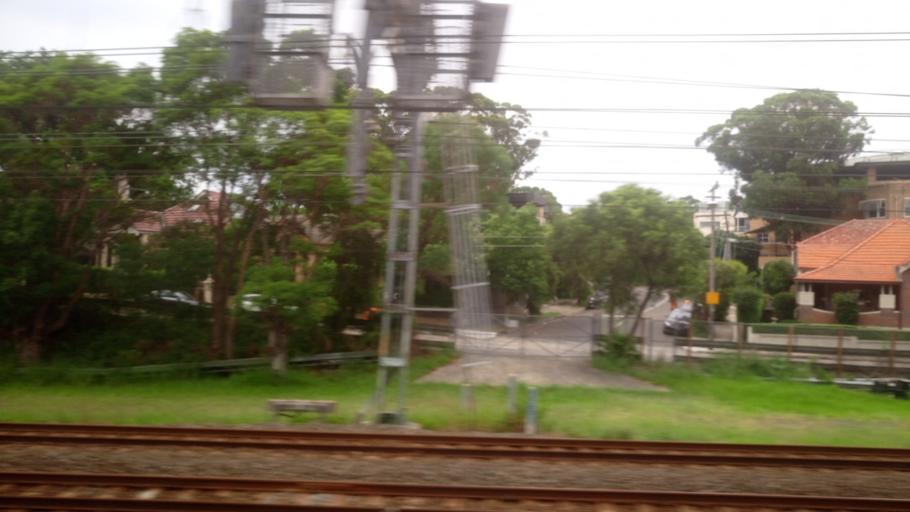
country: AU
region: New South Wales
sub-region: Marrickville
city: Camperdown
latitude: -33.8940
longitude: 151.1670
